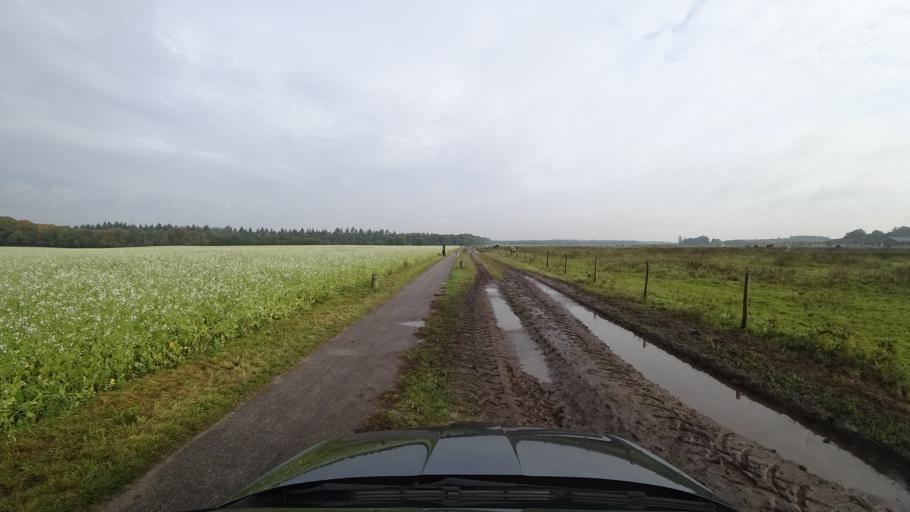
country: NL
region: Gelderland
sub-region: Gemeente Renkum
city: Heelsum
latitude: 51.9936
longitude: 5.7427
